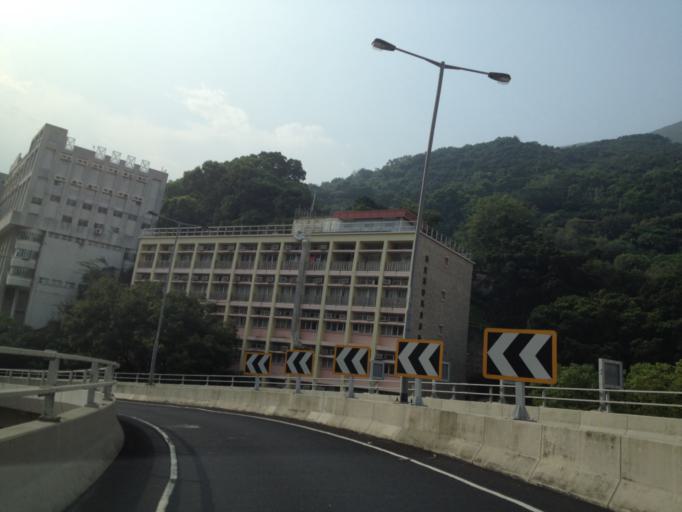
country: HK
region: Wanchai
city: Wan Chai
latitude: 22.2771
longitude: 114.2281
